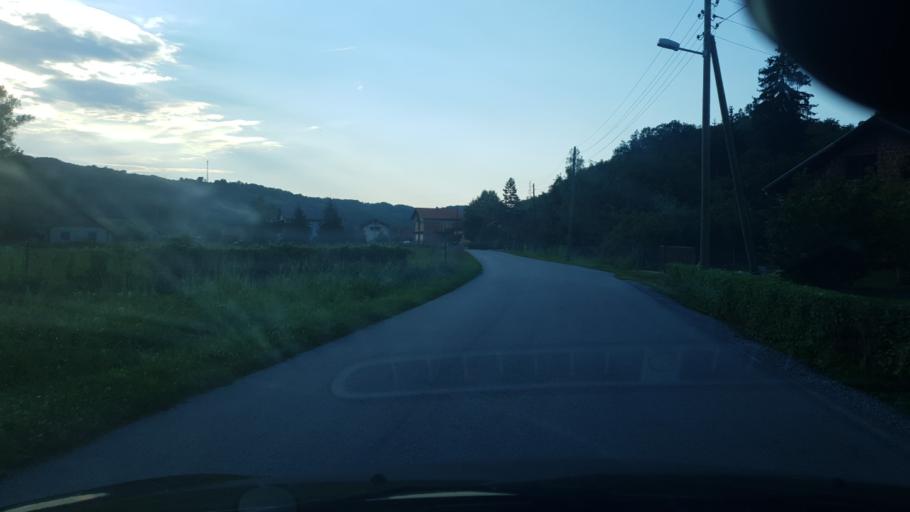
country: HR
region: Krapinsko-Zagorska
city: Zabok
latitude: 46.0349
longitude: 15.8971
